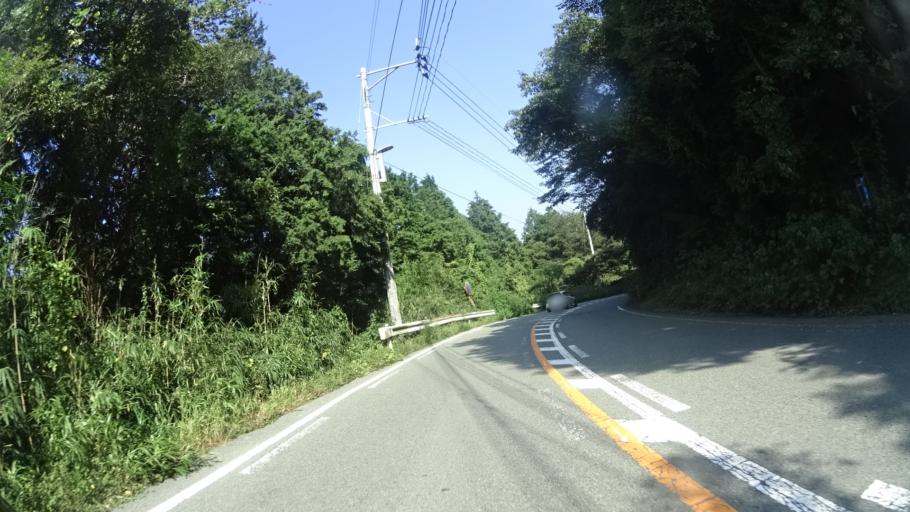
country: JP
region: Kumamoto
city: Ozu
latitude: 32.9028
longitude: 130.9423
